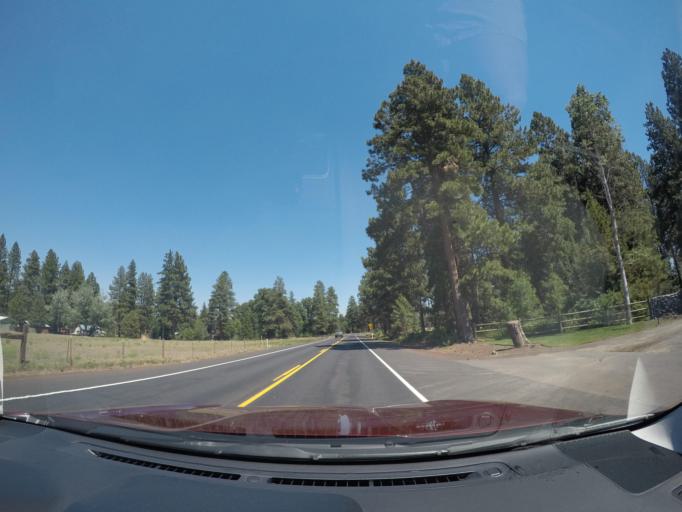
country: US
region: Oregon
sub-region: Deschutes County
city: Sisters
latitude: 44.2878
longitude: -121.5249
